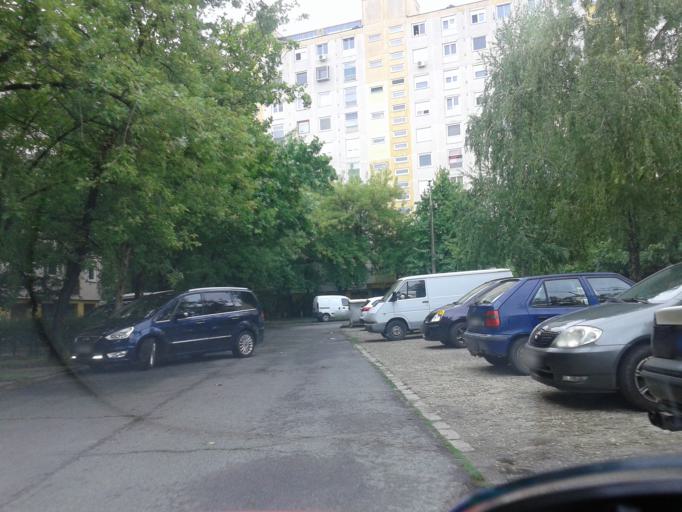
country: HU
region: Csongrad
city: Szeged
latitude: 46.2754
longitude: 20.1430
